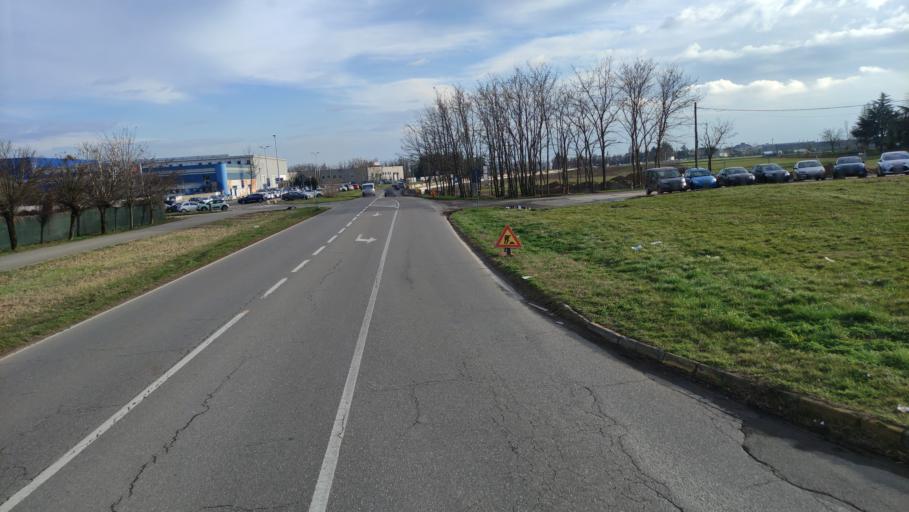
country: IT
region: Lombardy
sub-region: Provincia di Bergamo
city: Ghisalba
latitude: 45.5862
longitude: 9.7597
